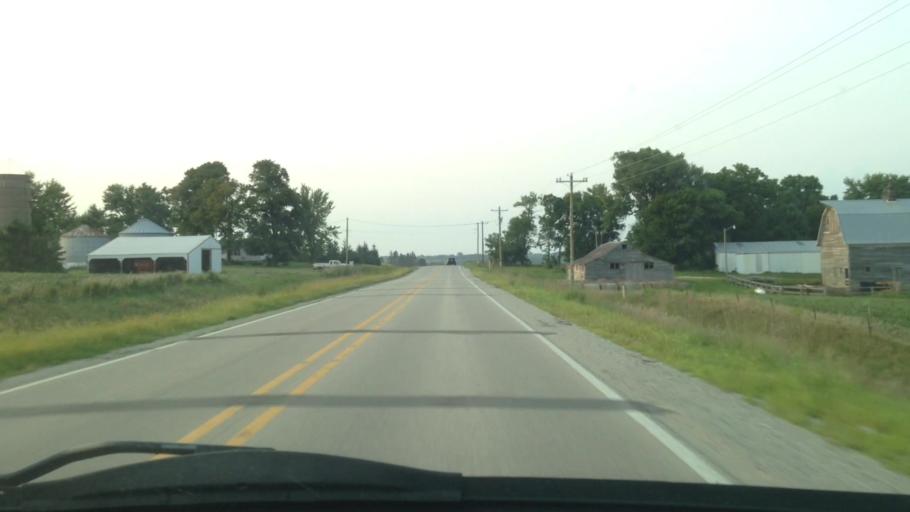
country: US
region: Iowa
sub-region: Linn County
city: Palo
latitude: 42.0777
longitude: -91.8690
